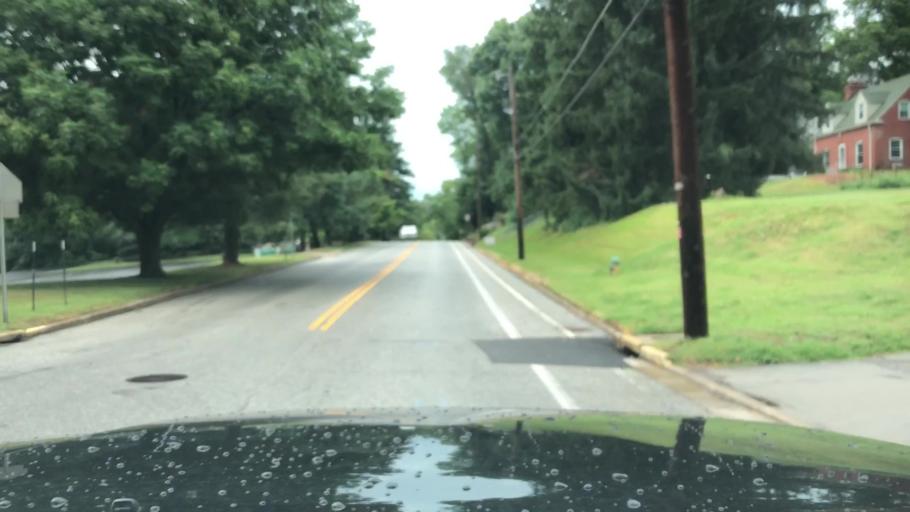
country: US
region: Missouri
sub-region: Saint Charles County
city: Saint Charles
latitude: 38.7900
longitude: -90.4971
